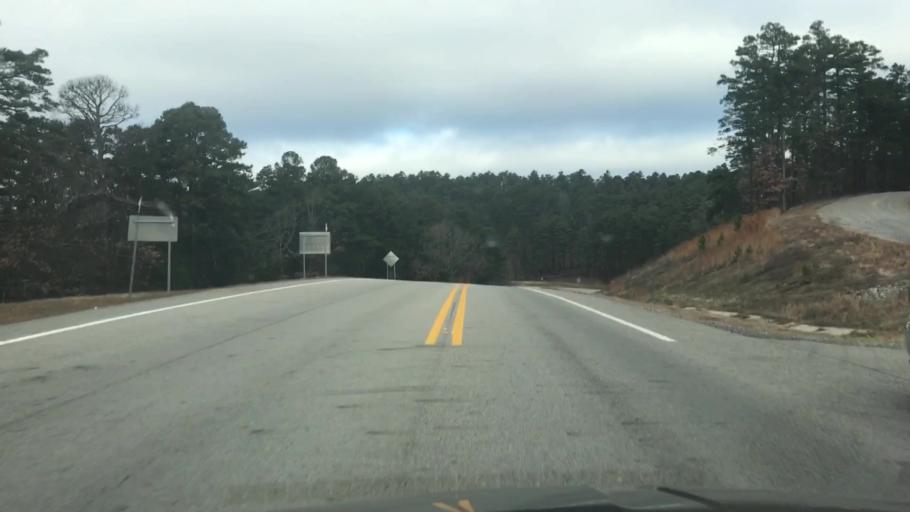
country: US
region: Arkansas
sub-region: Montgomery County
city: Mount Ida
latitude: 34.6810
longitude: -93.7884
